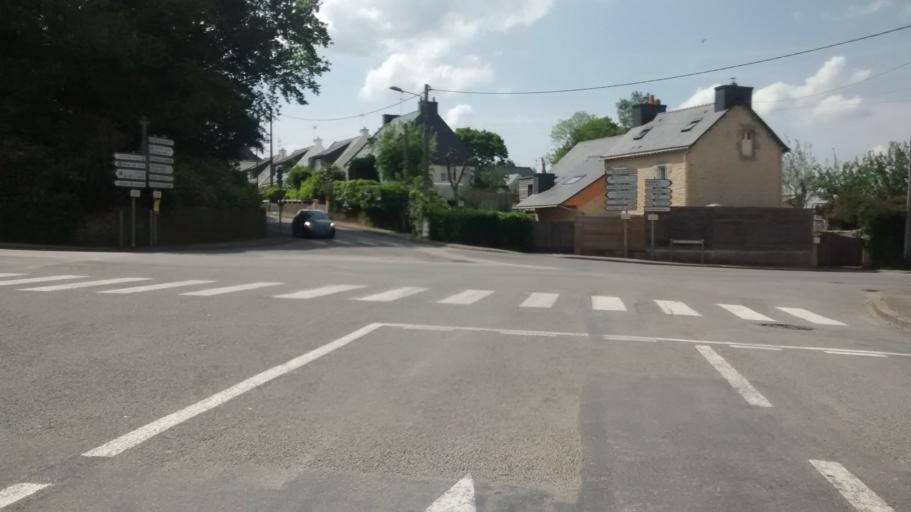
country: FR
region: Brittany
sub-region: Departement du Morbihan
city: Questembert
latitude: 47.6640
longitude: -2.4497
